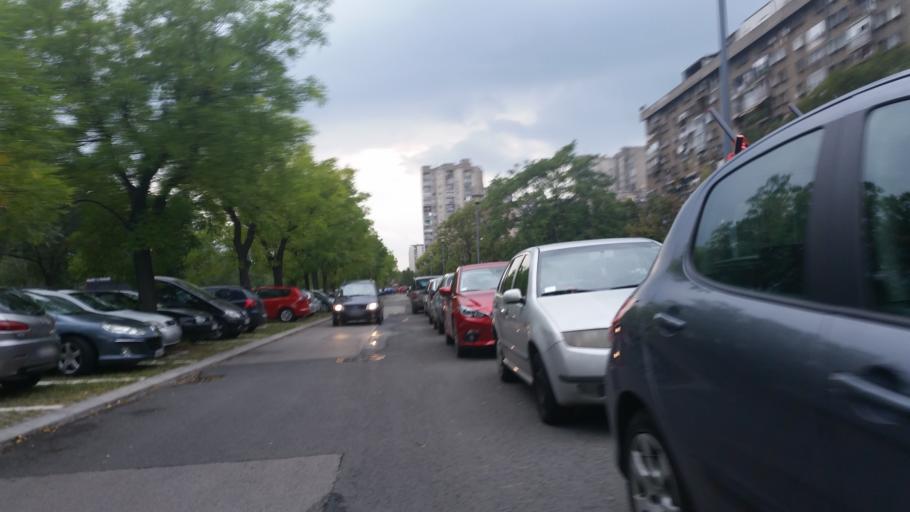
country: RS
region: Central Serbia
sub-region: Belgrade
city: Novi Beograd
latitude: 44.8114
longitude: 20.4140
